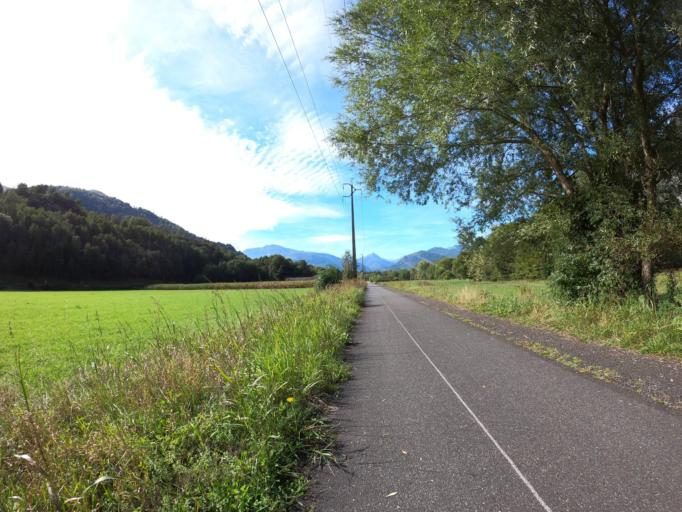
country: FR
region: Midi-Pyrenees
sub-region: Departement des Hautes-Pyrenees
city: Lourdes
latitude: 43.0459
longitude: -0.0536
